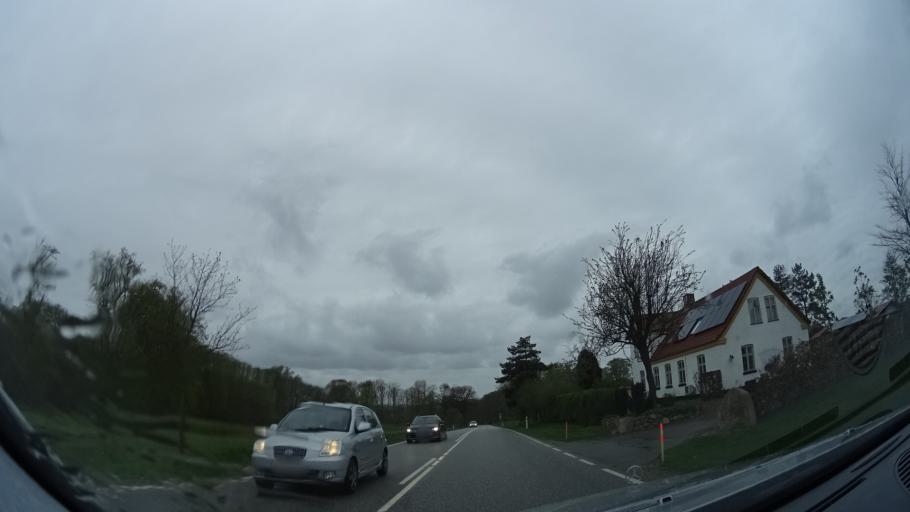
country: DK
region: Zealand
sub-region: Lejre Kommune
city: Ejby
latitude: 55.6736
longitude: 11.8216
